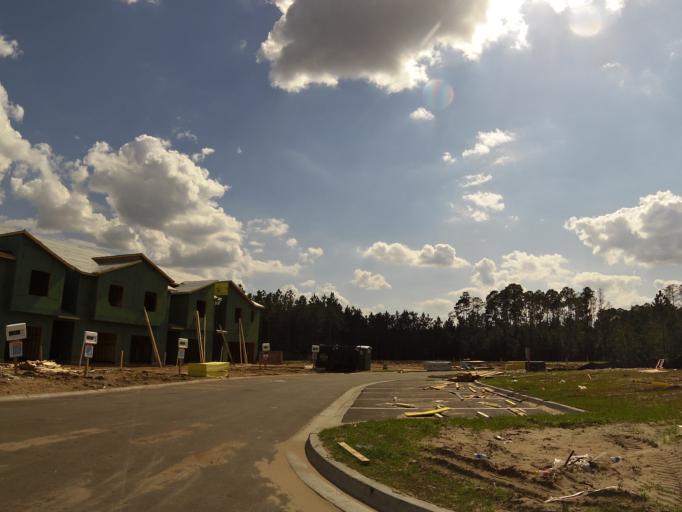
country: US
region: Florida
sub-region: Saint Johns County
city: Palm Valley
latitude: 30.2031
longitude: -81.5083
